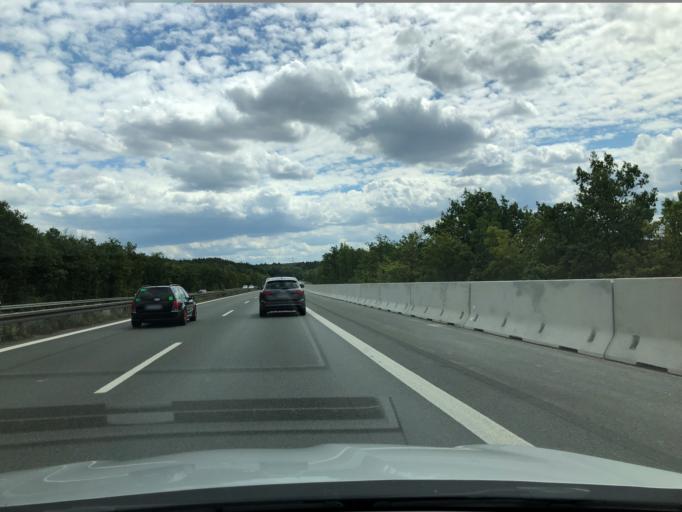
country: DE
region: Bavaria
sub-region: Regierungsbezirk Mittelfranken
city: Altdorf
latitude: 49.4046
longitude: 11.3652
